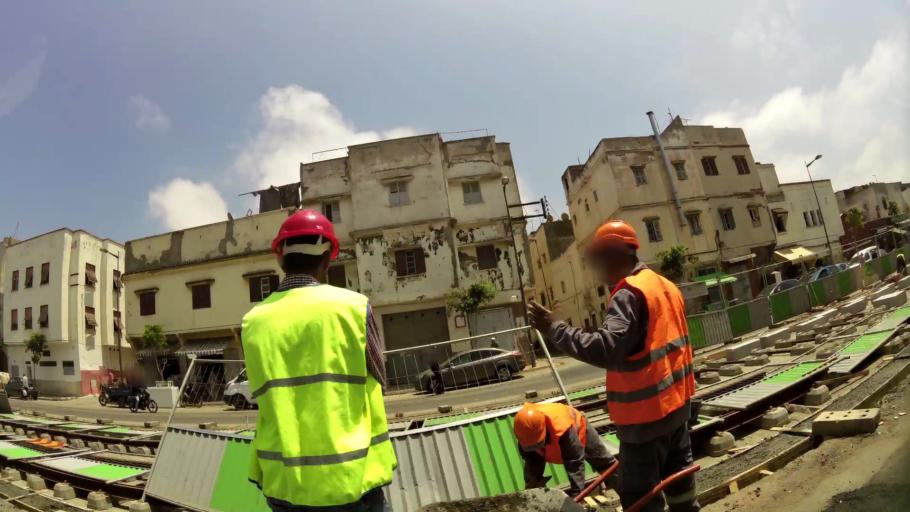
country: MA
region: Rabat-Sale-Zemmour-Zaer
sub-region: Rabat
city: Rabat
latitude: 34.0067
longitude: -6.8629
